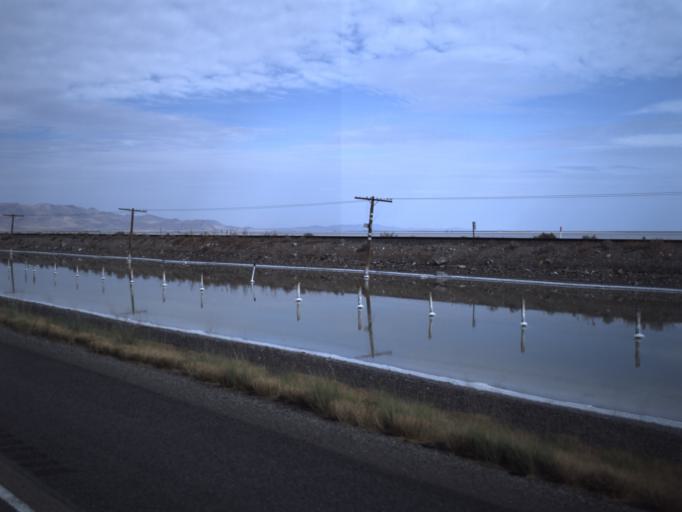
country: US
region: Utah
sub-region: Tooele County
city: Grantsville
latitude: 40.7313
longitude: -112.5916
